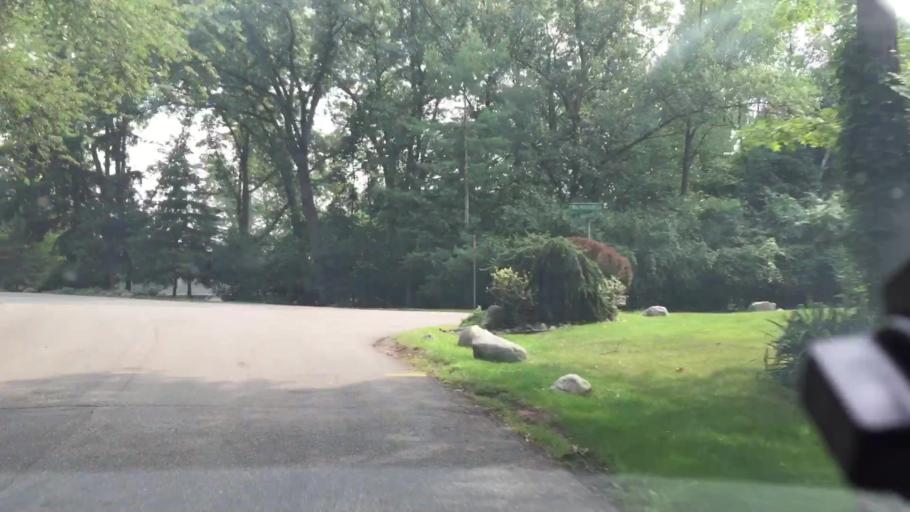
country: US
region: Michigan
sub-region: Oakland County
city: Sylvan Lake
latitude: 42.5968
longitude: -83.2917
